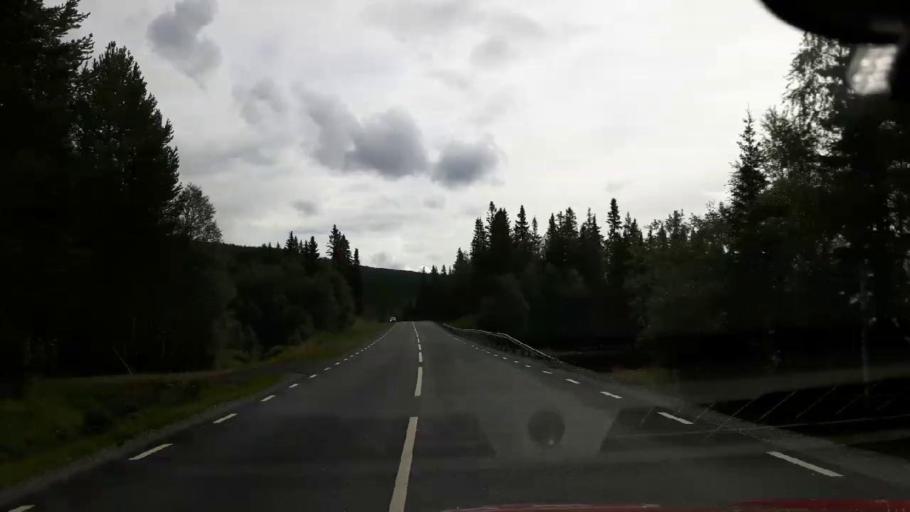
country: NO
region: Nord-Trondelag
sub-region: Lierne
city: Sandvika
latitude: 64.6484
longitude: 14.1390
